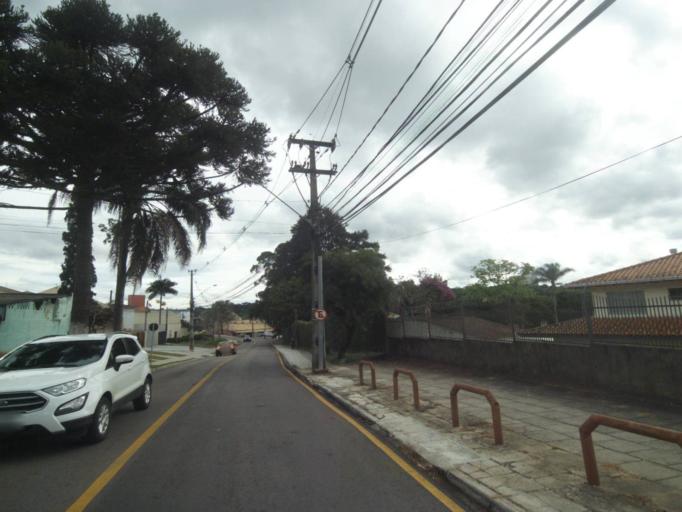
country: BR
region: Parana
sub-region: Curitiba
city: Curitiba
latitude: -25.4403
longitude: -49.3134
